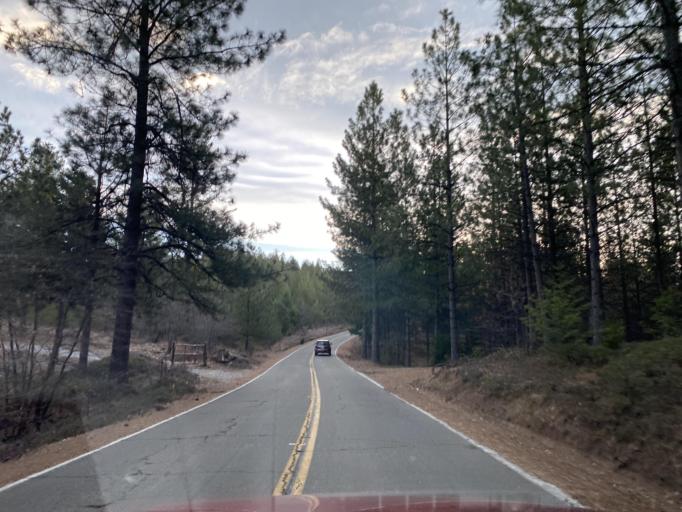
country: US
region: California
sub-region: Amador County
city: Pioneer
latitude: 38.4983
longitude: -120.6017
